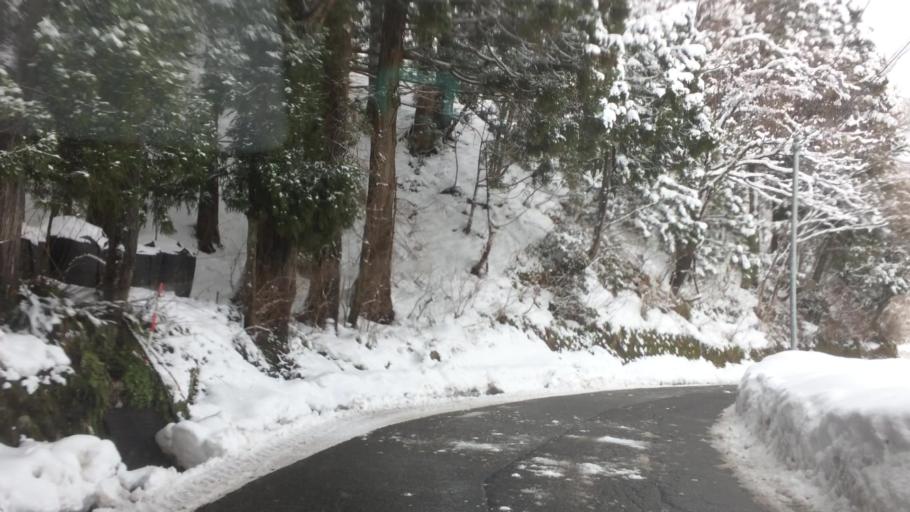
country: JP
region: Toyama
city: Kamiichi
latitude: 36.5699
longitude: 137.3747
